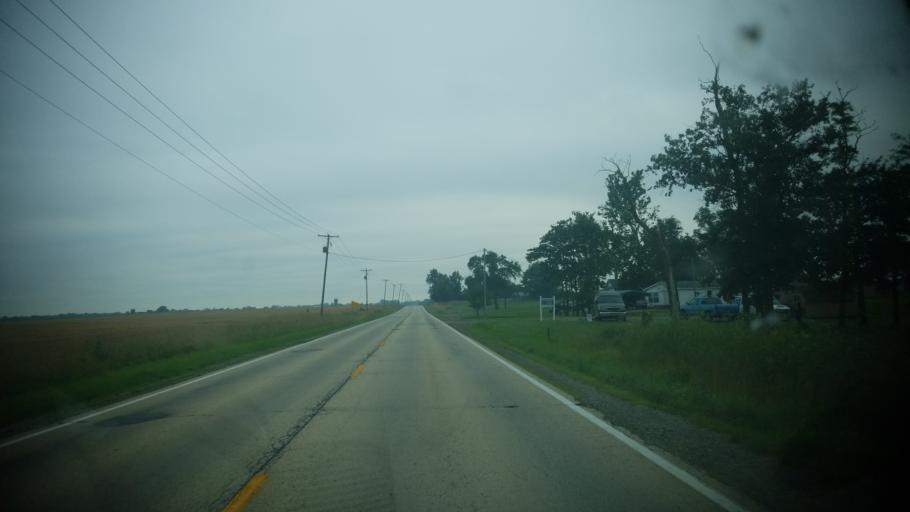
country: US
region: Illinois
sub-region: Clay County
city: Flora
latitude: 38.6549
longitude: -88.4384
